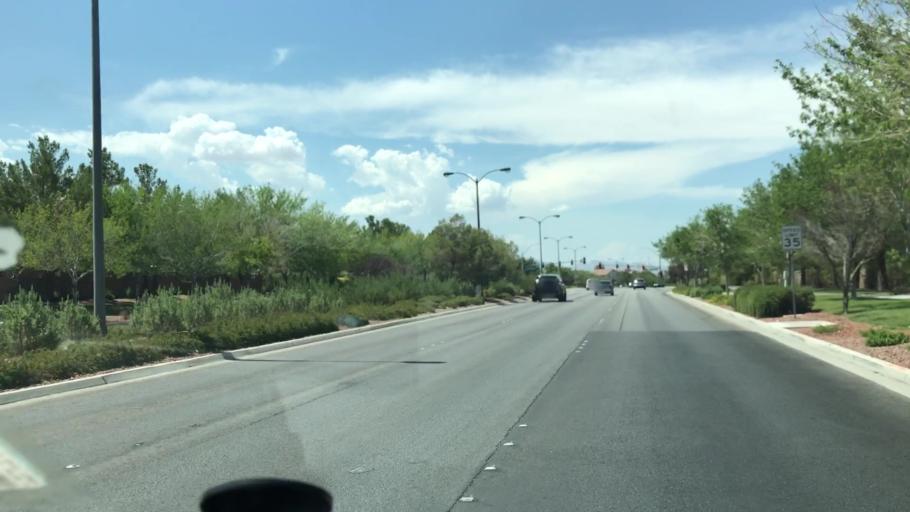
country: US
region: Nevada
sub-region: Clark County
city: Enterprise
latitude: 35.9926
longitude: -115.2055
